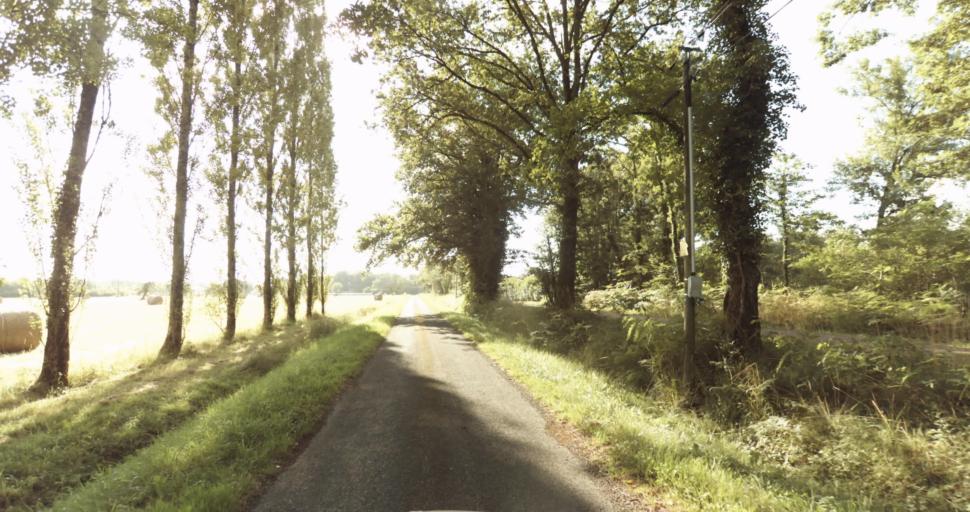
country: FR
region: Aquitaine
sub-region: Departement de la Gironde
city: Bazas
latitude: 44.4428
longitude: -0.2487
